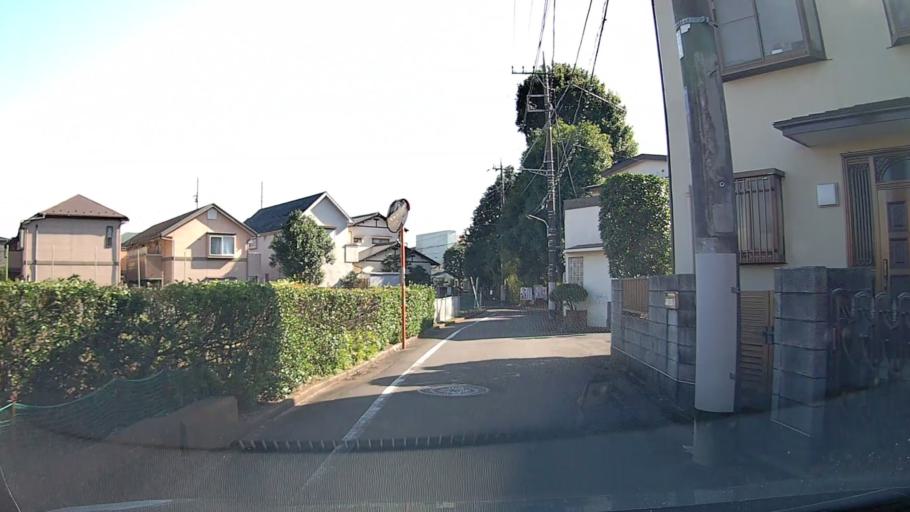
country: JP
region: Tokyo
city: Musashino
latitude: 35.7379
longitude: 139.5865
